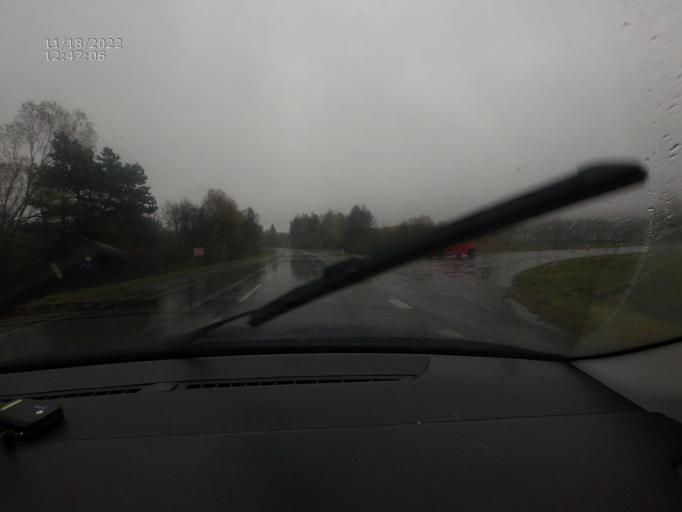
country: CZ
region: Plzensky
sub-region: Okres Klatovy
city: Kolinec
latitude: 49.3421
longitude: 13.4324
